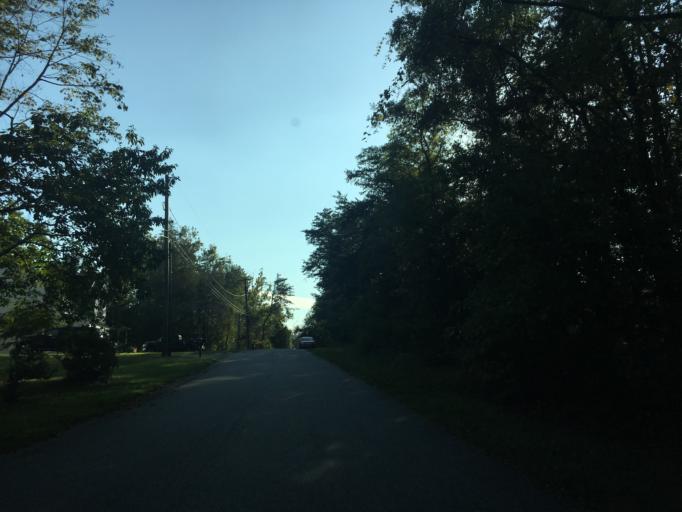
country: US
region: Maryland
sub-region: Anne Arundel County
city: Jessup
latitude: 39.1730
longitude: -76.7523
